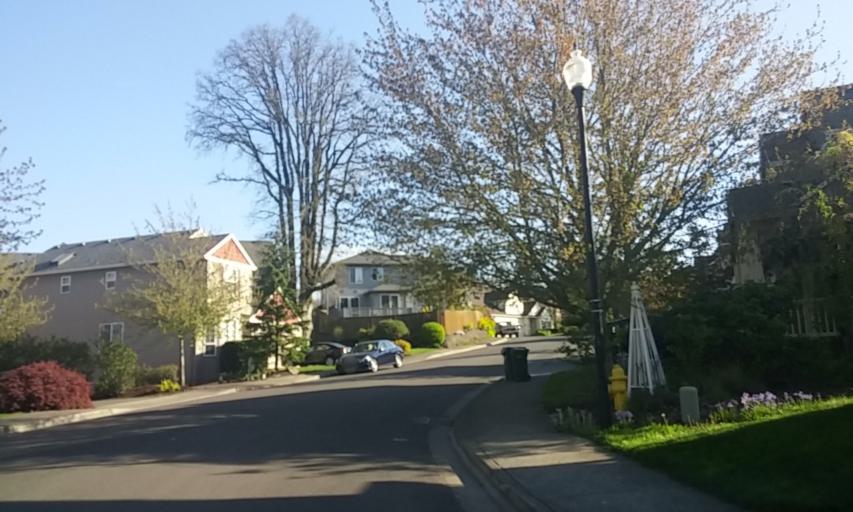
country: US
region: Oregon
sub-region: Washington County
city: Cedar Mill
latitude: 45.5461
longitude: -122.7957
